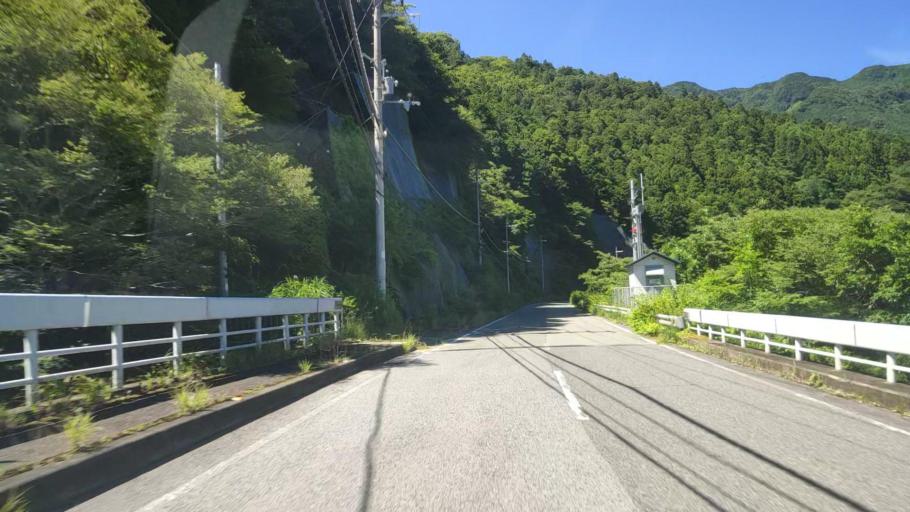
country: JP
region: Nara
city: Yoshino-cho
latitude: 34.3254
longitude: 135.9687
